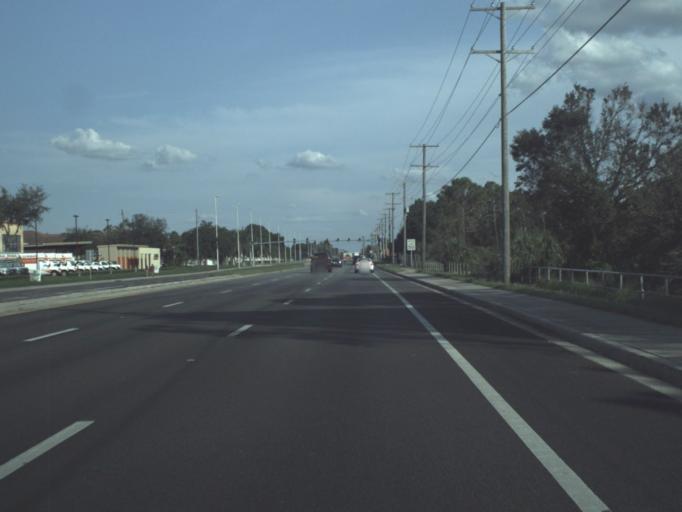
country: US
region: Florida
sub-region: Hillsborough County
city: Town 'n' Country
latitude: 28.0133
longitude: -82.6130
